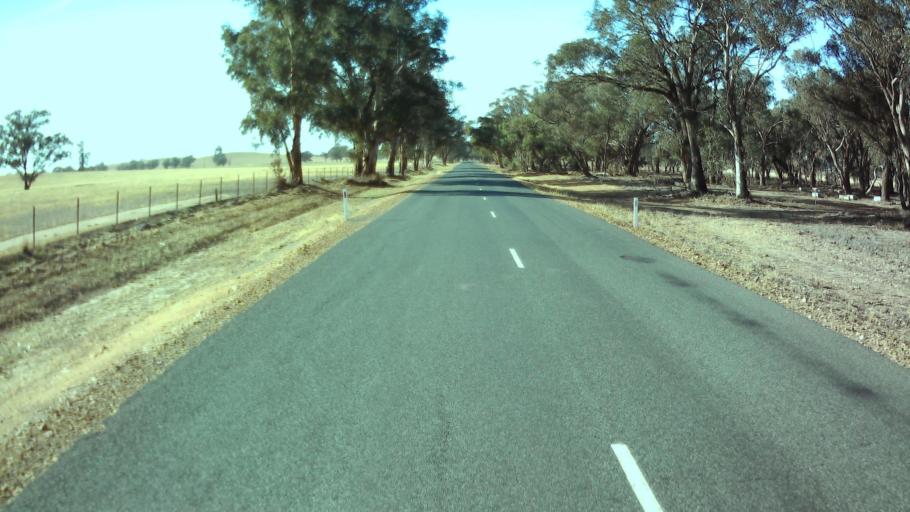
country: AU
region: New South Wales
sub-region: Weddin
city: Grenfell
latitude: -33.9522
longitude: 148.1387
